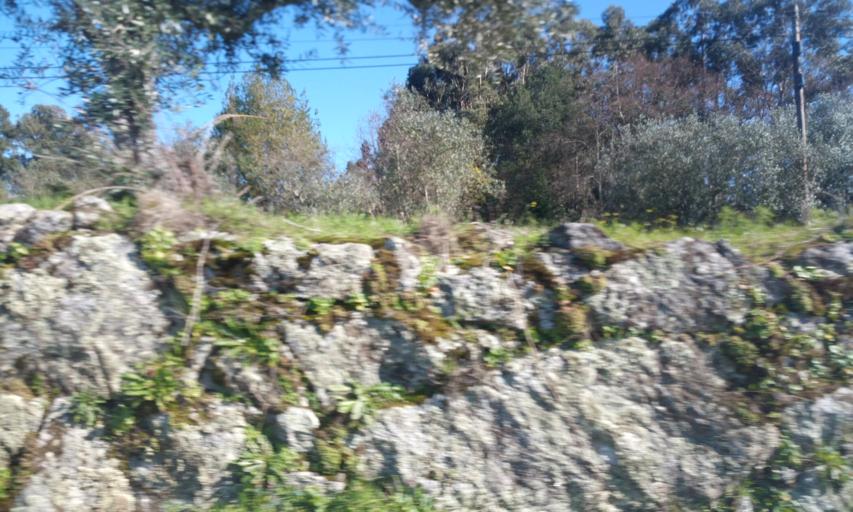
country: PT
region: Guarda
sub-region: Manteigas
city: Manteigas
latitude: 40.5072
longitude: -7.6091
